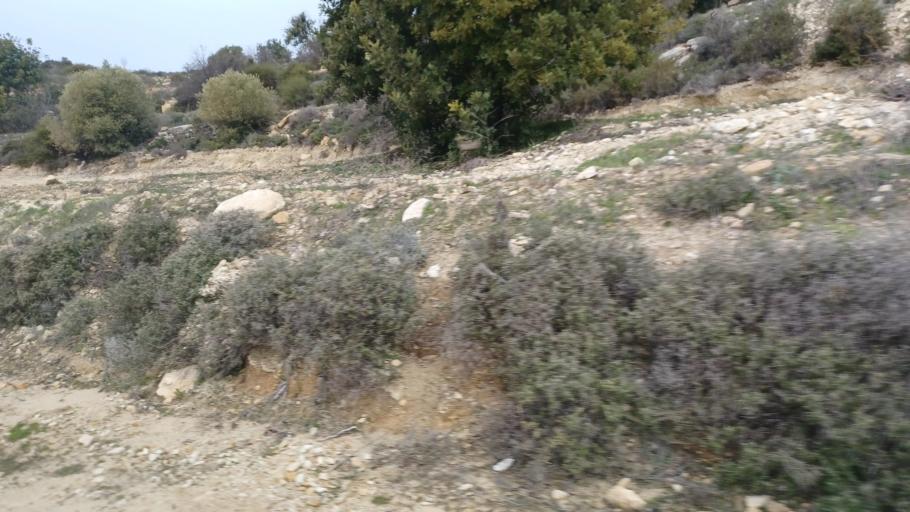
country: CY
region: Limassol
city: Pachna
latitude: 34.7694
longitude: 32.7594
